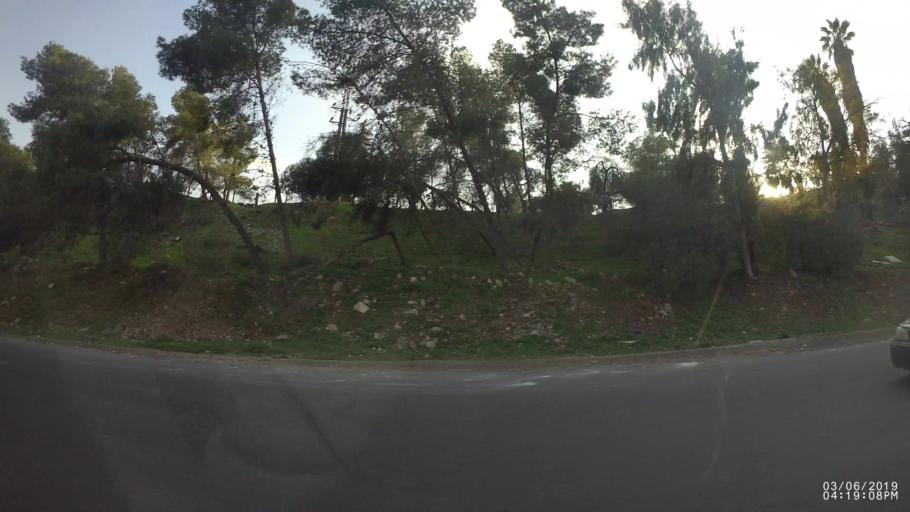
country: JO
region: Amman
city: Amman
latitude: 31.9809
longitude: 35.9713
